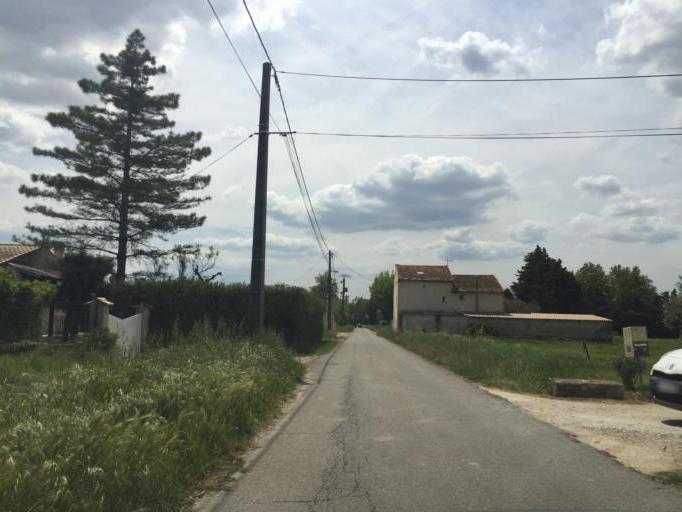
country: FR
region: Provence-Alpes-Cote d'Azur
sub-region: Departement du Vaucluse
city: Jonquieres
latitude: 44.1213
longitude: 4.8798
